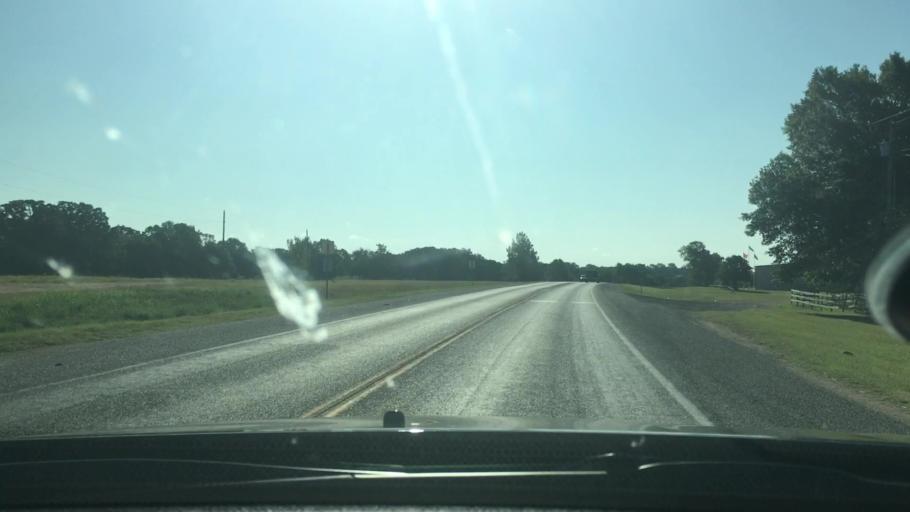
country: US
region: Oklahoma
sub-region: Johnston County
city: Tishomingo
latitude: 34.2413
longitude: -96.7476
